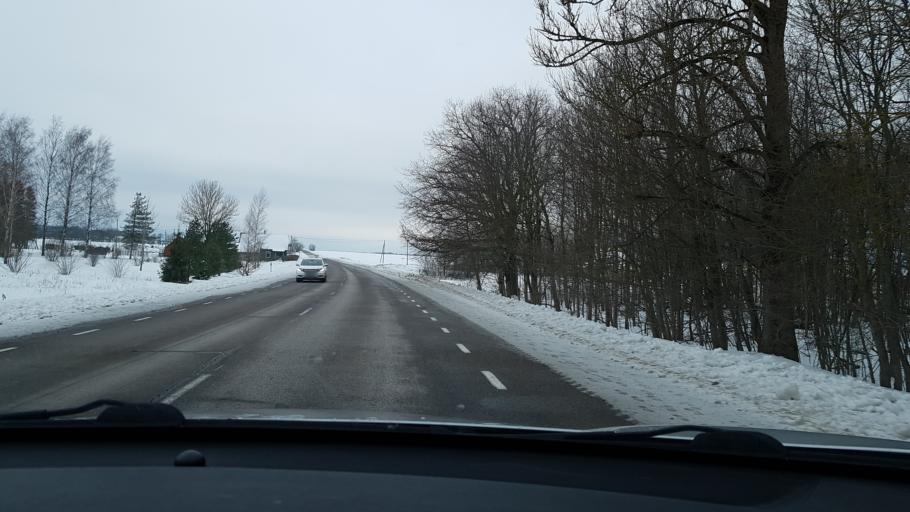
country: EE
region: Jaervamaa
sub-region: Paide linn
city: Paide
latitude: 58.8978
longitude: 25.7441
